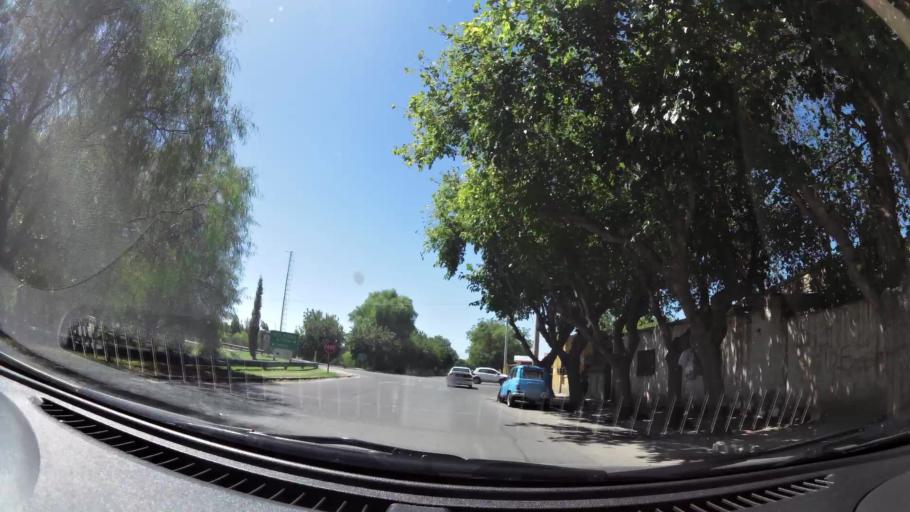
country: AR
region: San Juan
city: San Juan
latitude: -31.5176
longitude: -68.5294
